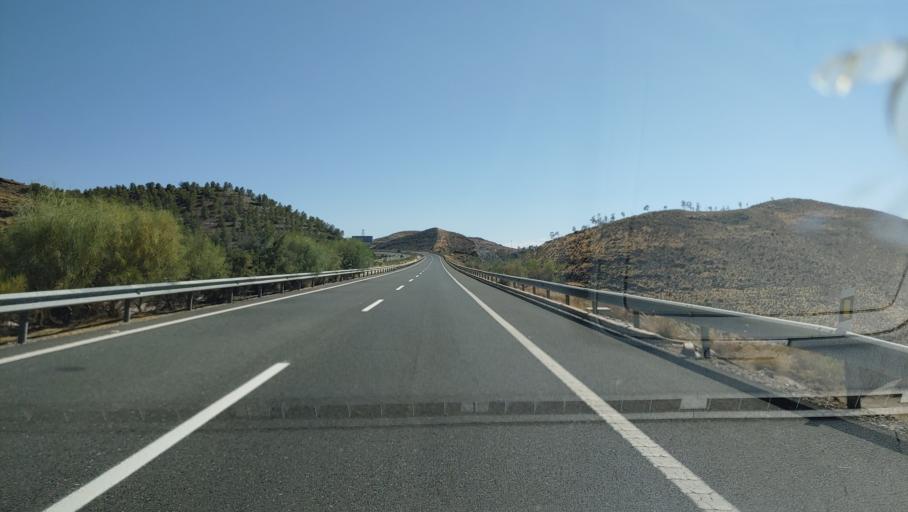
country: ES
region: Andalusia
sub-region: Provincia de Almeria
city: Gergal
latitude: 37.1027
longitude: -2.5286
